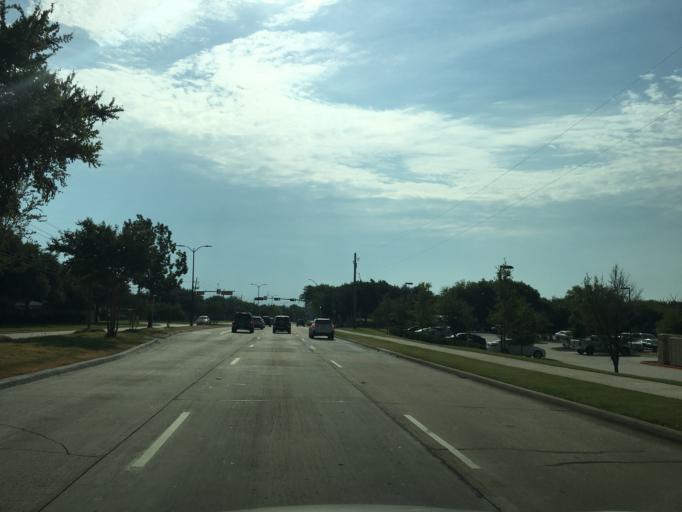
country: US
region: Texas
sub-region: Collin County
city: Fairview
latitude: 33.1986
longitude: -96.6891
